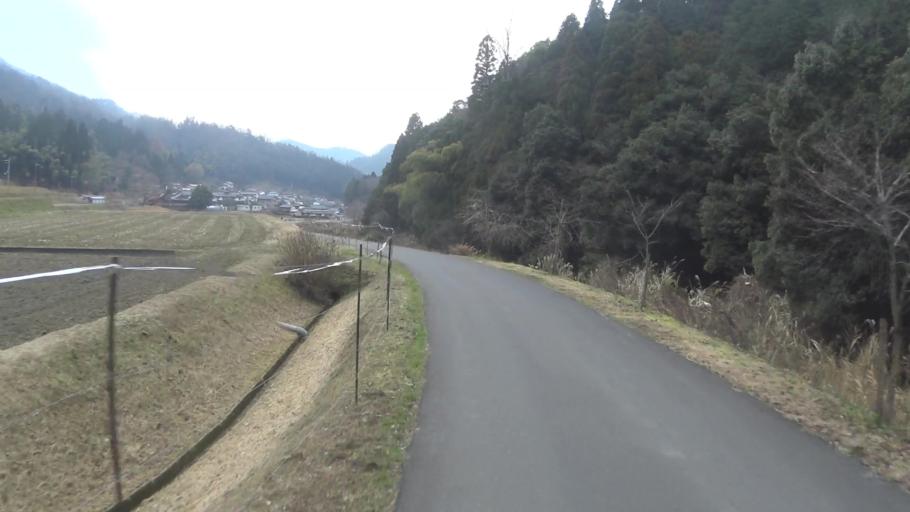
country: JP
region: Kyoto
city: Maizuru
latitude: 35.4442
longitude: 135.4355
